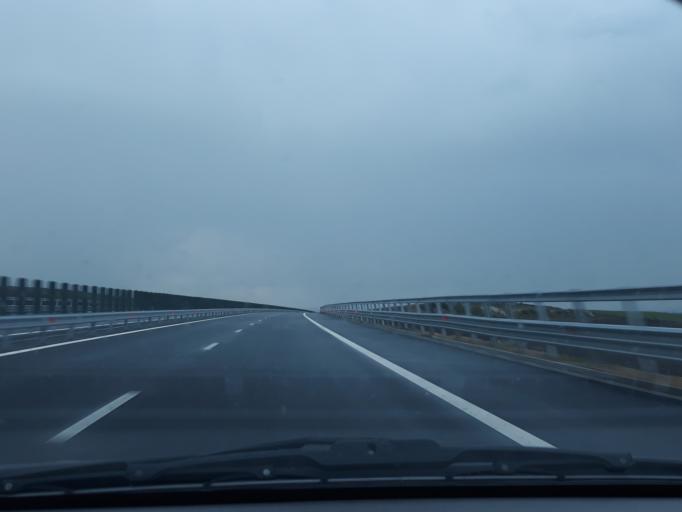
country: RO
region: Mures
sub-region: Comuna Ogra
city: Ogra
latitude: 46.4382
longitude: 24.3328
